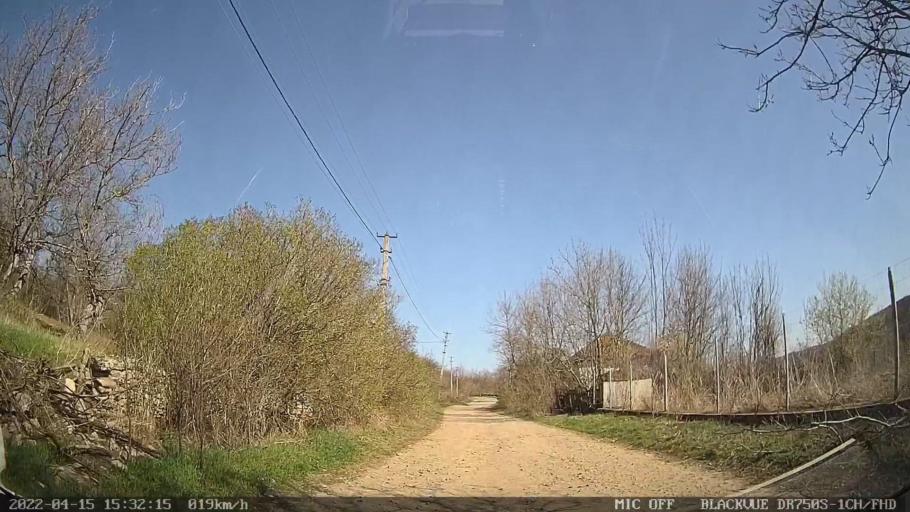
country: MD
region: Raionul Ocnita
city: Otaci
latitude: 48.3512
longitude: 27.9195
